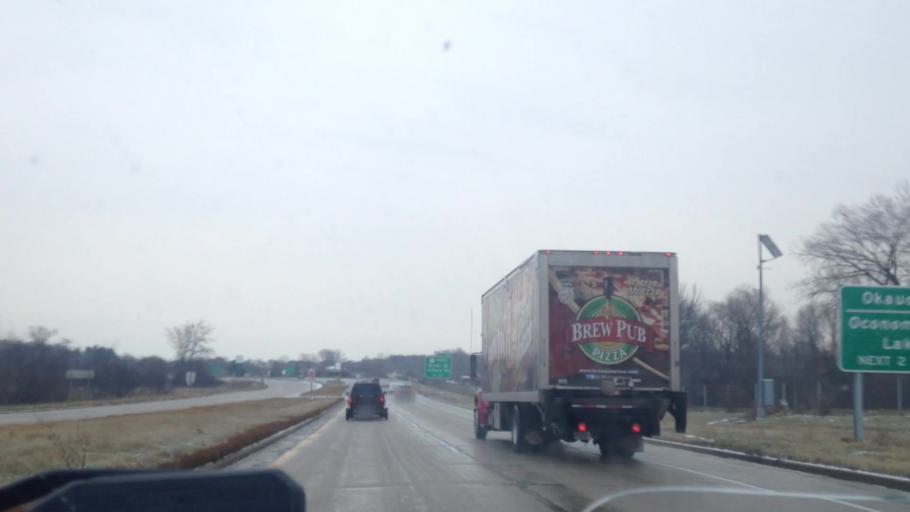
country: US
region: Wisconsin
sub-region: Waukesha County
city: Oconomowoc
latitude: 43.1068
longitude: -88.4738
